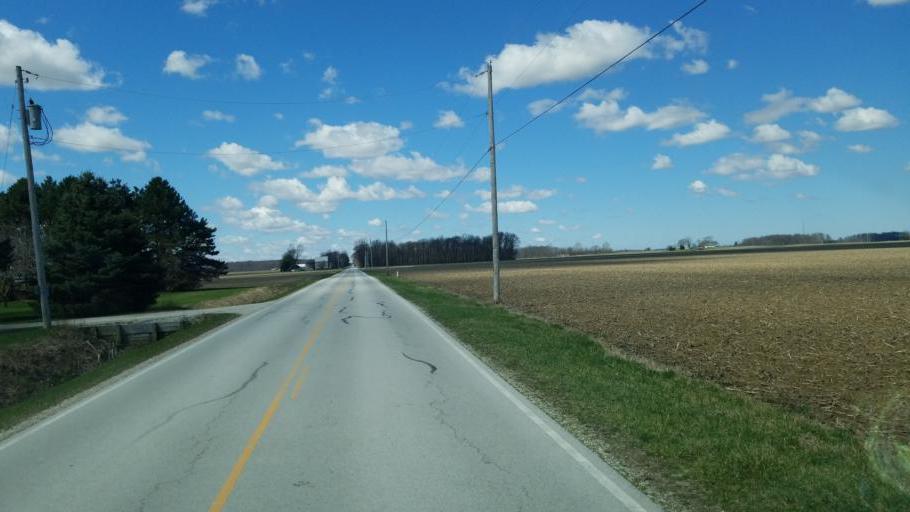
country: US
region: Ohio
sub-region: Sandusky County
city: Green Springs
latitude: 41.2567
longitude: -83.0866
